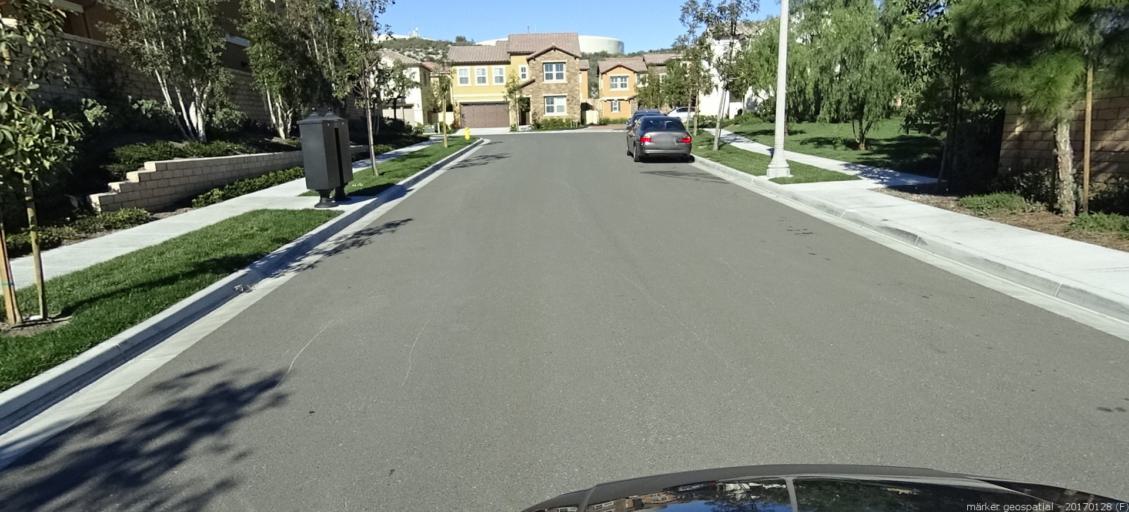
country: US
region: California
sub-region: Orange County
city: Foothill Ranch
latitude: 33.6708
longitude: -117.6737
